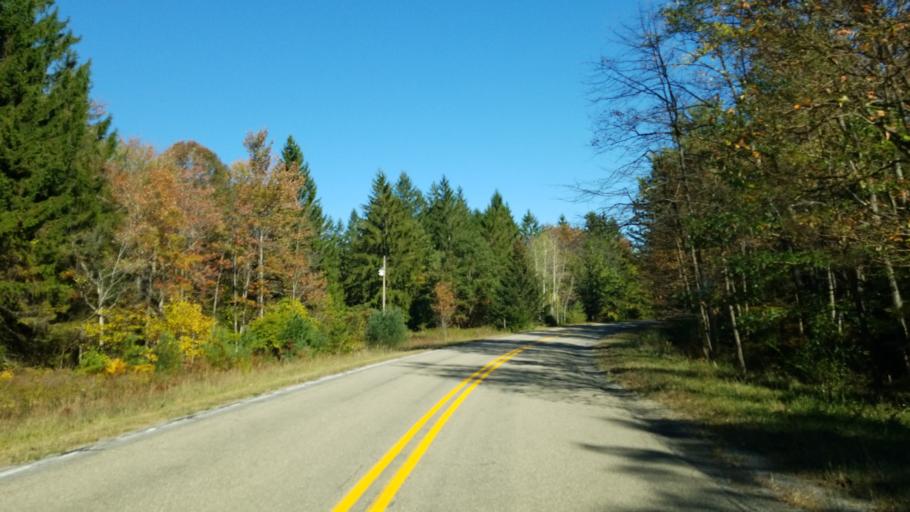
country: US
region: Pennsylvania
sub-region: Clearfield County
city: Shiloh
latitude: 41.2618
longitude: -78.2984
